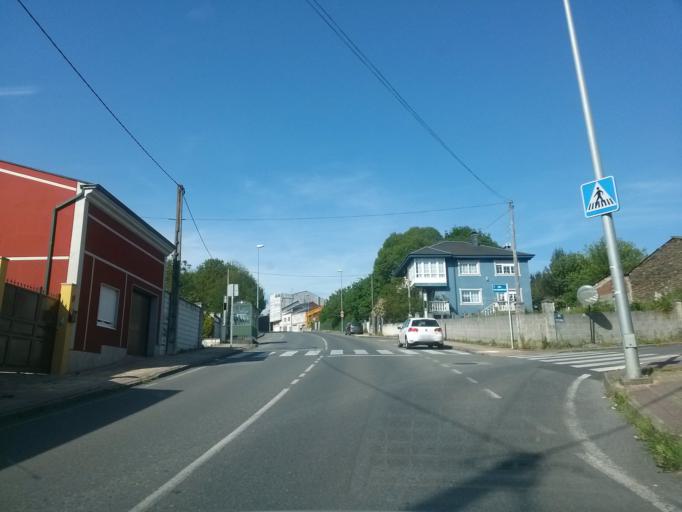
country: ES
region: Galicia
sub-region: Provincia de Lugo
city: Lugo
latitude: 43.0306
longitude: -7.5606
